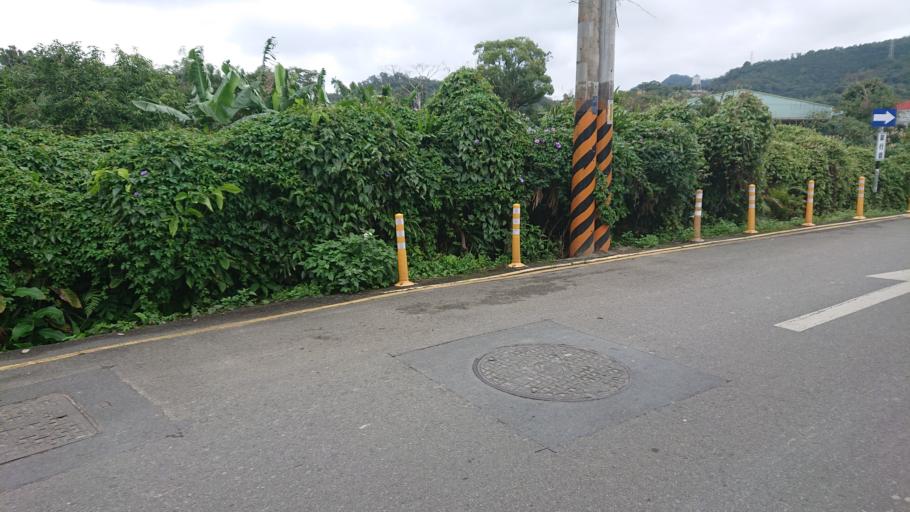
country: TW
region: Taipei
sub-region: Taipei
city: Banqiao
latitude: 24.9616
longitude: 121.4426
